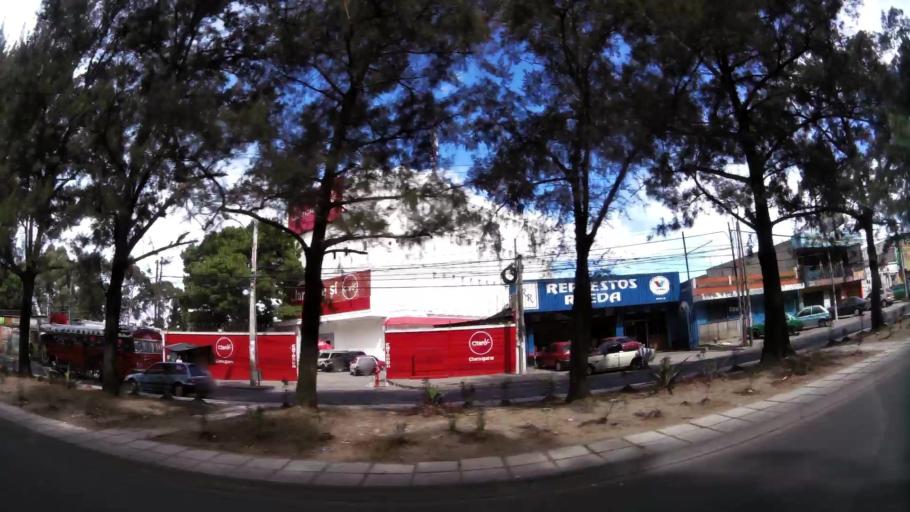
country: GT
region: Guatemala
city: Mixco
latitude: 14.6478
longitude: -90.5812
